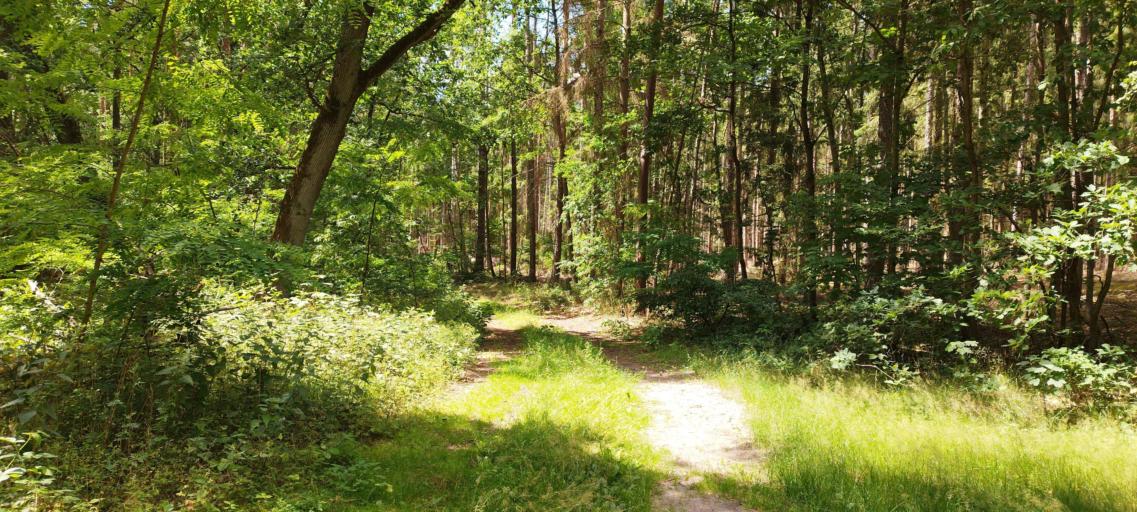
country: DE
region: Brandenburg
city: Reichenwalde
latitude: 52.2964
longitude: 14.0175
